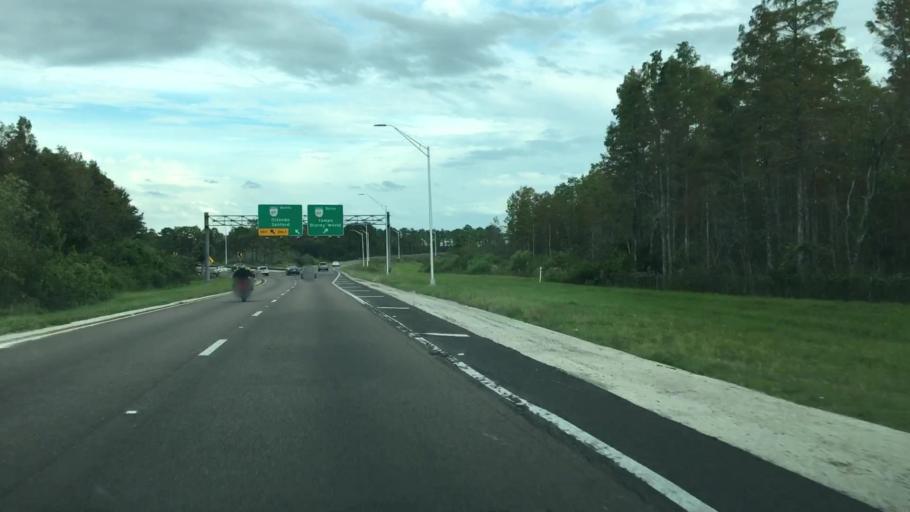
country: US
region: Florida
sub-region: Orange County
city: Conway
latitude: 28.4506
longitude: -81.2360
